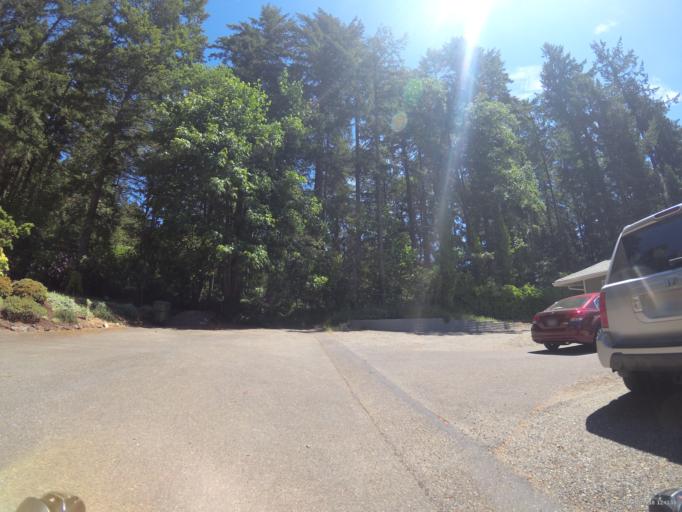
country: US
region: Washington
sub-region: Pierce County
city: University Place
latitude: 47.2039
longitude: -122.5534
